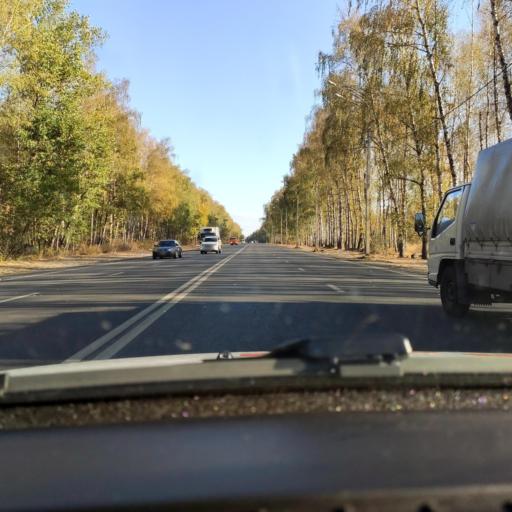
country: RU
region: Voronezj
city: Pridonskoy
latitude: 51.6940
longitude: 39.0927
